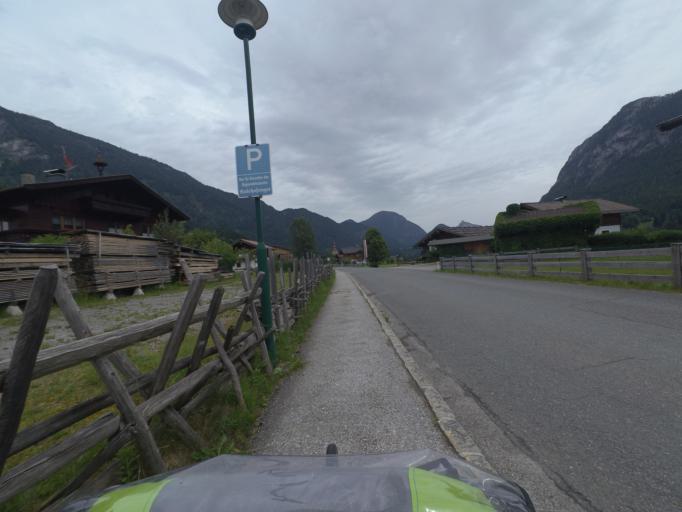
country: AT
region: Salzburg
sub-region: Politischer Bezirk Zell am See
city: Unken
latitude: 47.6463
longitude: 12.7237
